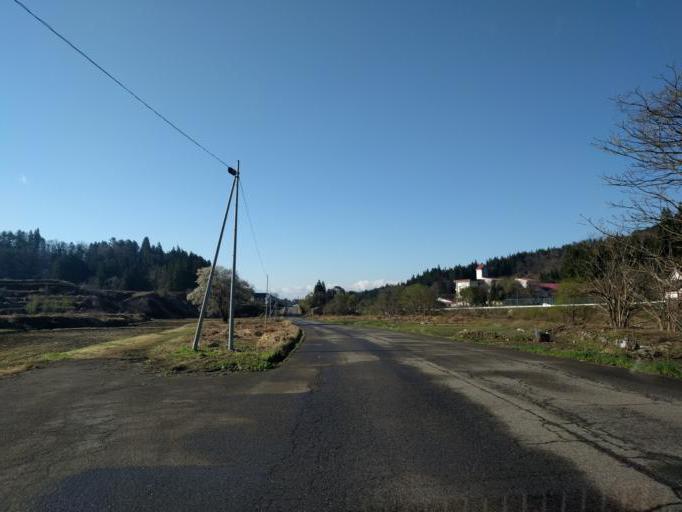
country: JP
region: Fukushima
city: Kitakata
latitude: 37.7214
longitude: 139.7805
